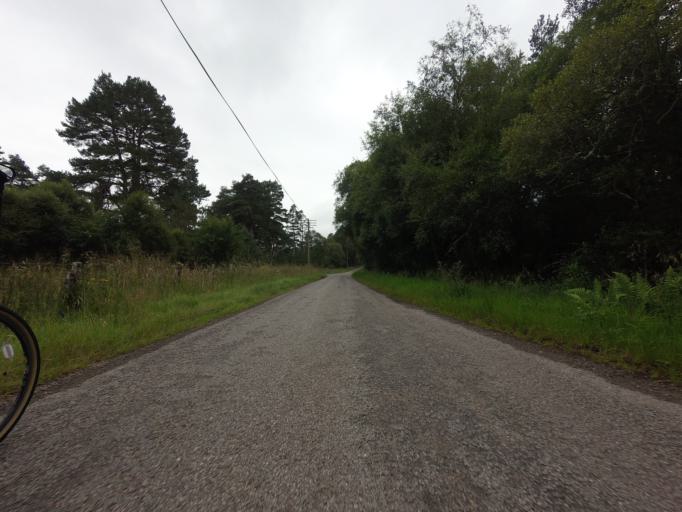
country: GB
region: Scotland
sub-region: Highland
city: Alness
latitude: 57.9878
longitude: -4.4120
